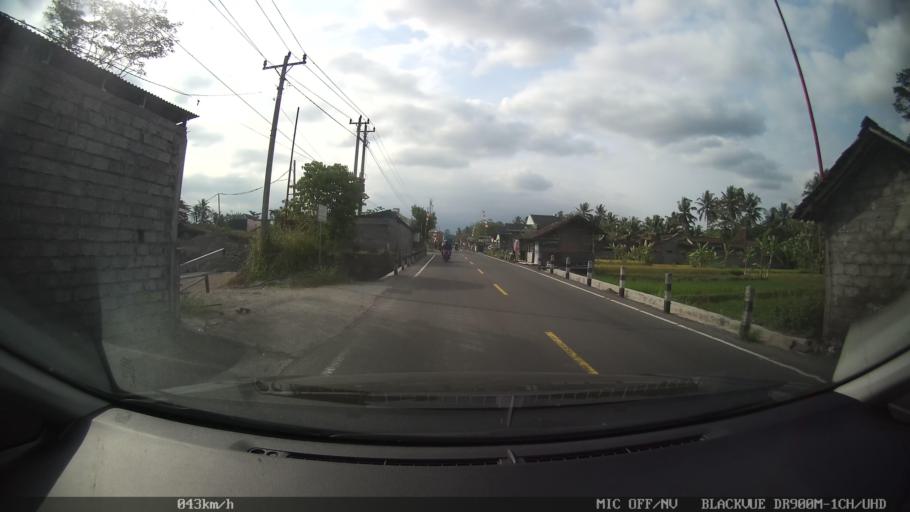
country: ID
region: Central Java
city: Candi Prambanan
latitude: -7.6852
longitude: 110.4605
